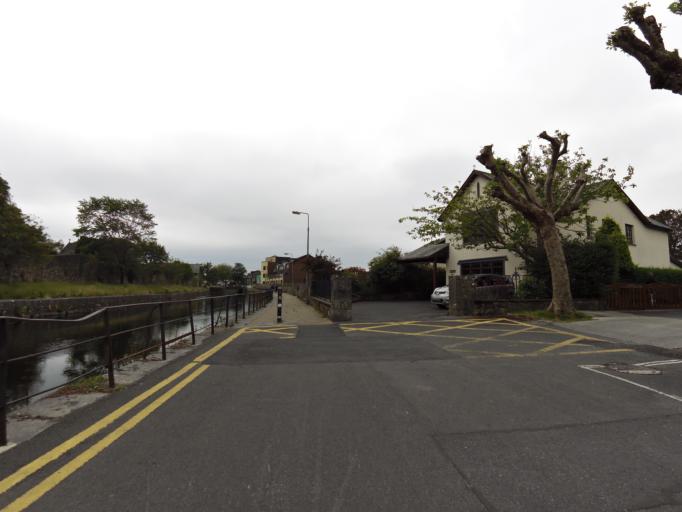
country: IE
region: Connaught
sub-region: County Galway
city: Gaillimh
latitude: 53.2747
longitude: -9.0613
